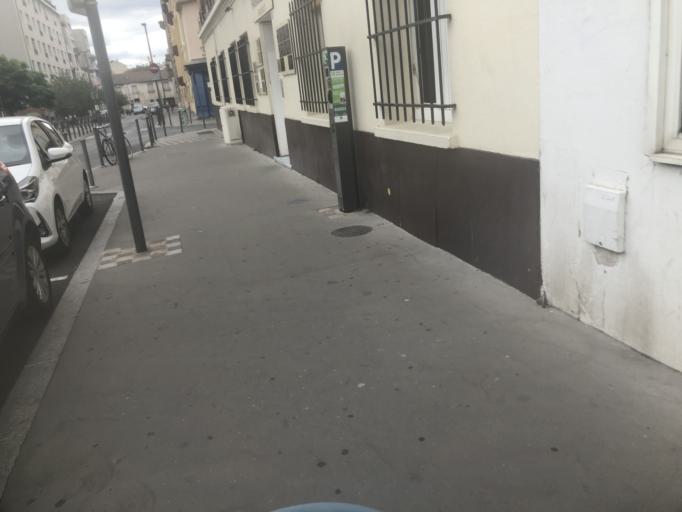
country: FR
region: Ile-de-France
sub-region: Paris
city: Saint-Ouen
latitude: 48.9090
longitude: 2.3348
